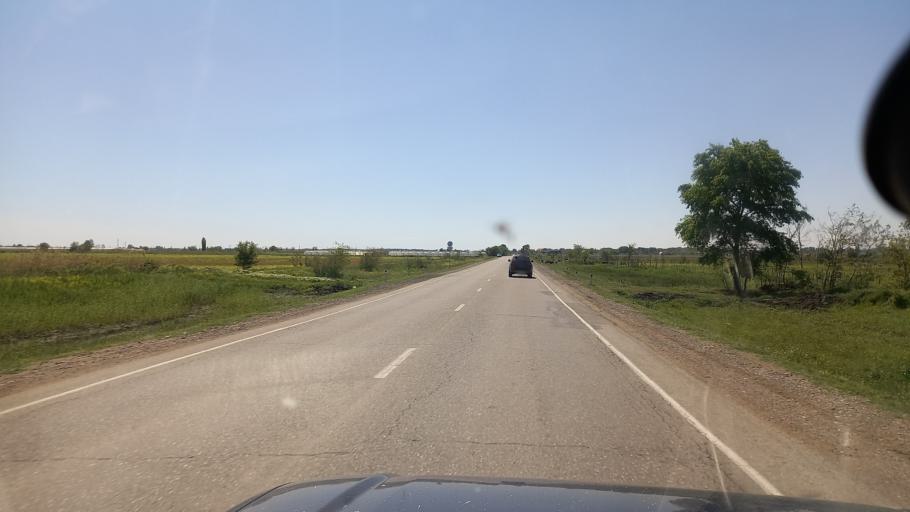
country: RU
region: Dagestan
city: Belidzhi
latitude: 41.8719
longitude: 48.3550
